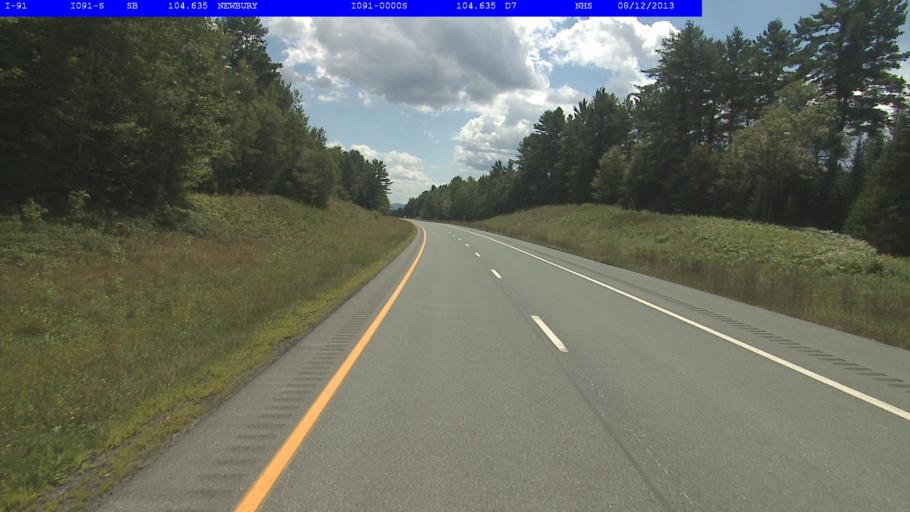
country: US
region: New Hampshire
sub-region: Grafton County
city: Haverhill
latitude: 44.0806
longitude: -72.1139
